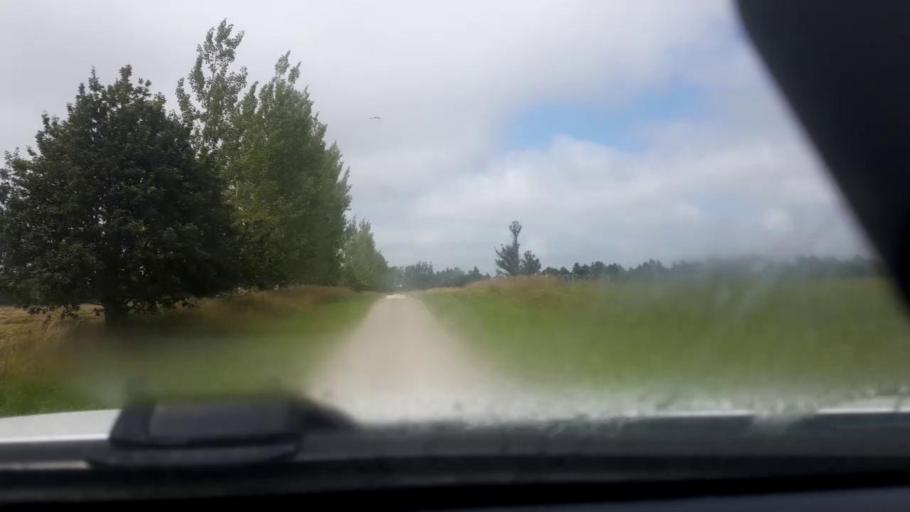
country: NZ
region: Canterbury
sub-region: Timaru District
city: Pleasant Point
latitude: -44.1988
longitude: 171.0907
